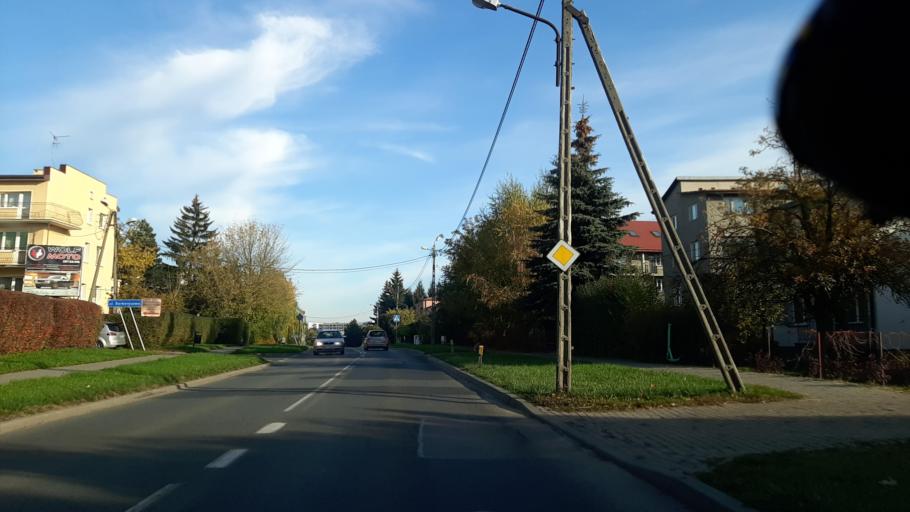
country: PL
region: Lublin Voivodeship
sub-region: Powiat lubelski
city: Lublin
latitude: 51.2656
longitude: 22.5816
